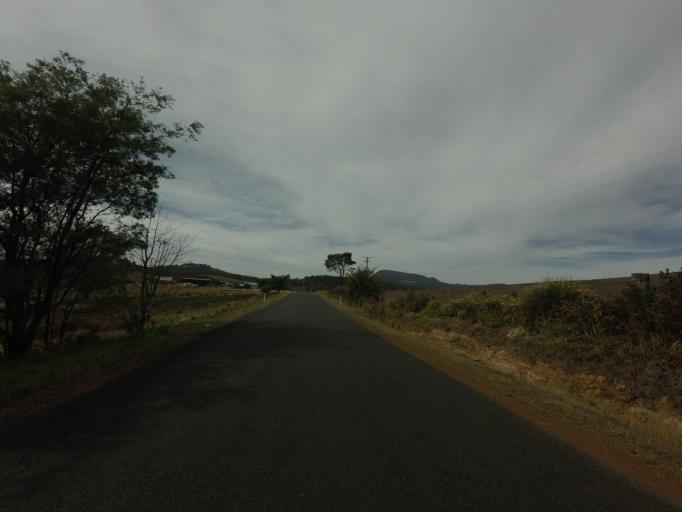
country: AU
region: Tasmania
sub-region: Sorell
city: Sorell
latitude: -42.4509
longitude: 147.5709
